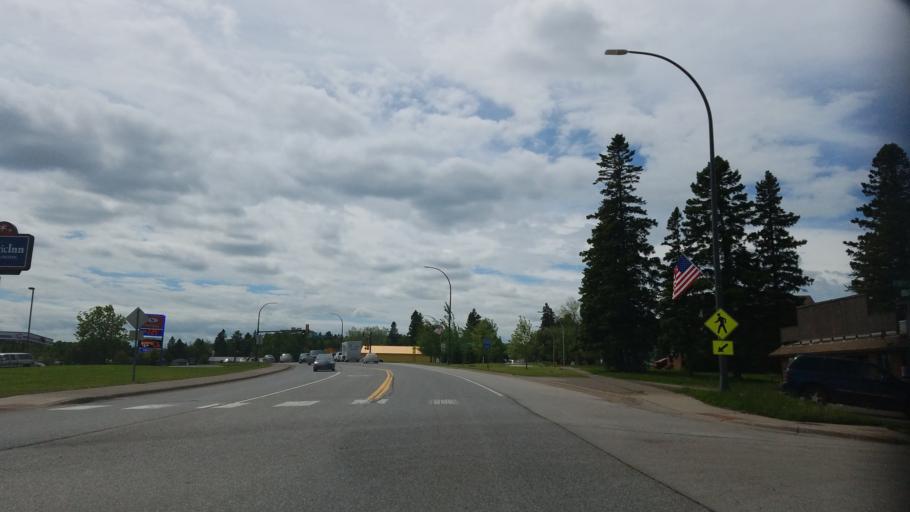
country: US
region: Minnesota
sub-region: Lake County
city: Two Harbors
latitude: 47.0256
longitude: -91.6875
